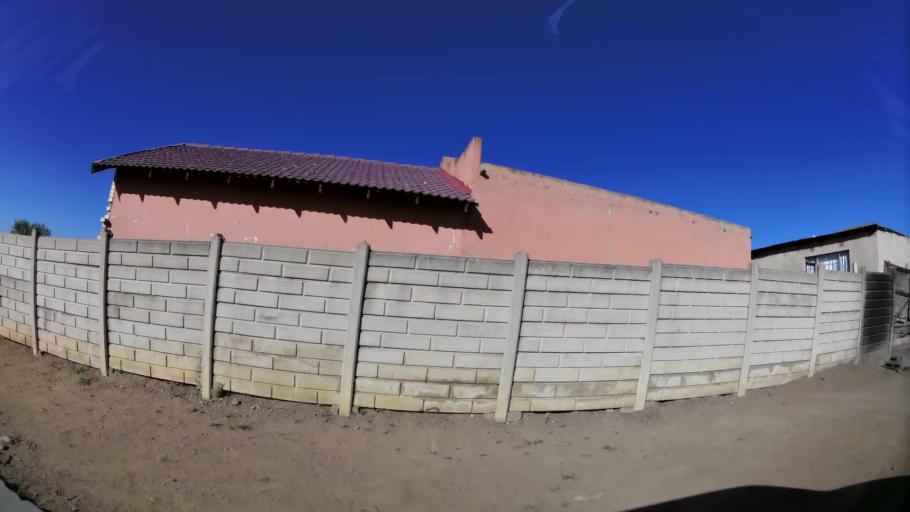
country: ZA
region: Gauteng
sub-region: Ekurhuleni Metropolitan Municipality
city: Tembisa
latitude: -26.0207
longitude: 28.2173
